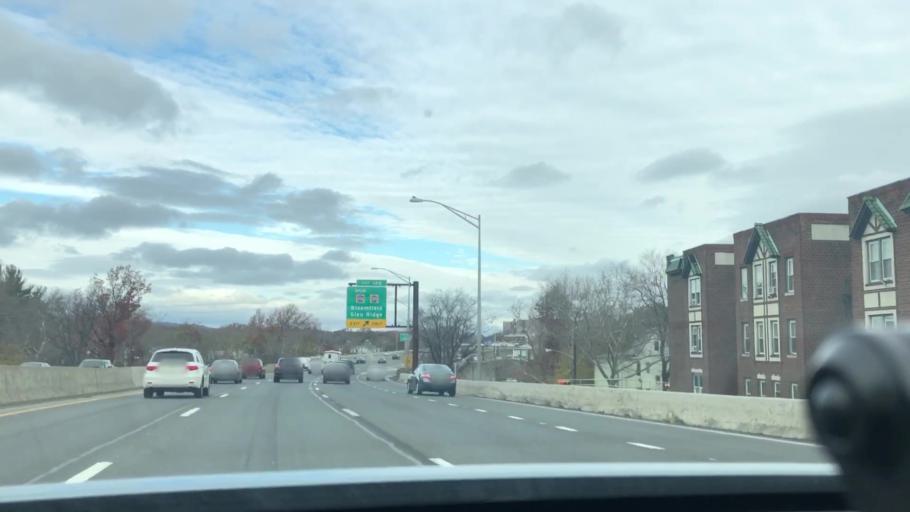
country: US
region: New Jersey
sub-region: Essex County
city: East Orange
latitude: 40.7813
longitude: -74.2012
